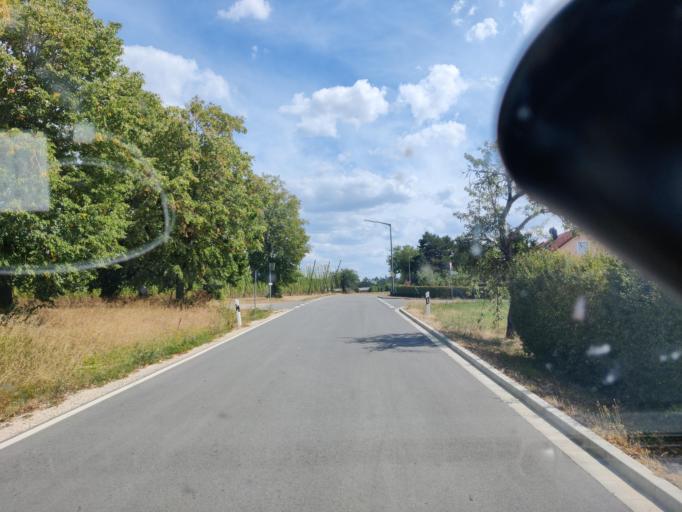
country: DE
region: Bavaria
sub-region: Regierungsbezirk Mittelfranken
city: Heideck
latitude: 49.1219
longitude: 11.1305
